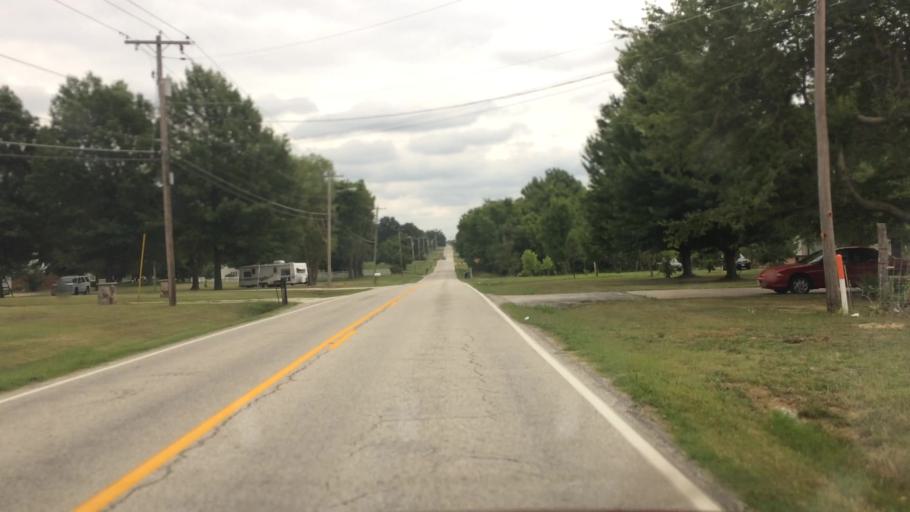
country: US
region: Missouri
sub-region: Greene County
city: Springfield
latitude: 37.2952
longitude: -93.2582
